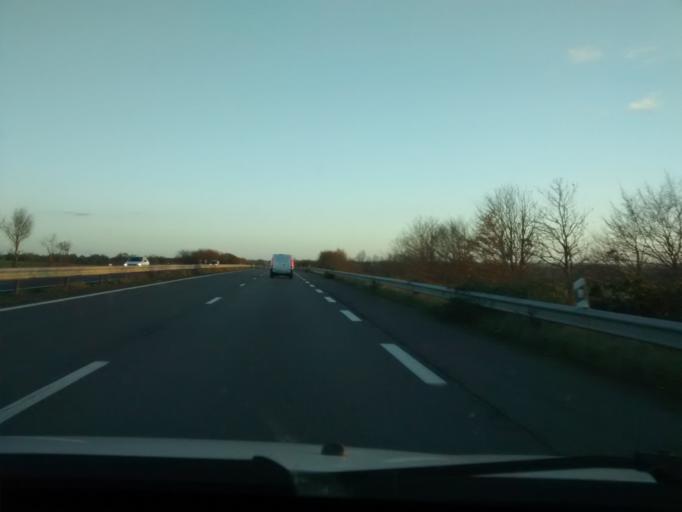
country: FR
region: Brittany
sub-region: Departement d'Ille-et-Vilaine
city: Pleugueneuc
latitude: 48.3893
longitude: -1.9060
